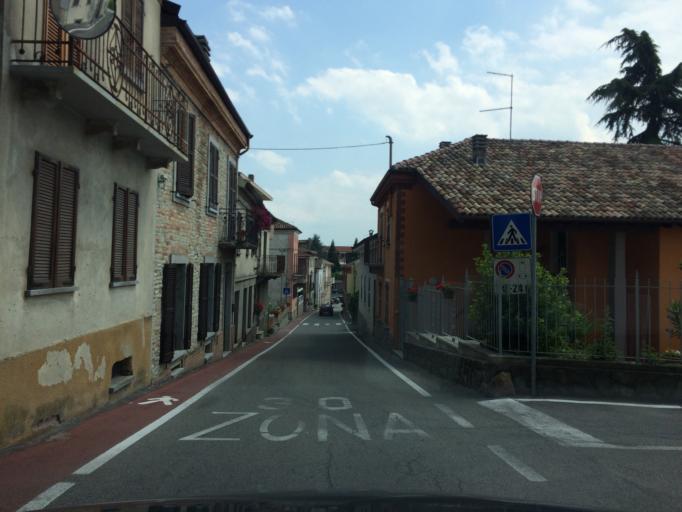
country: IT
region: Piedmont
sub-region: Provincia di Asti
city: Calosso
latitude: 44.7388
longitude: 8.2285
